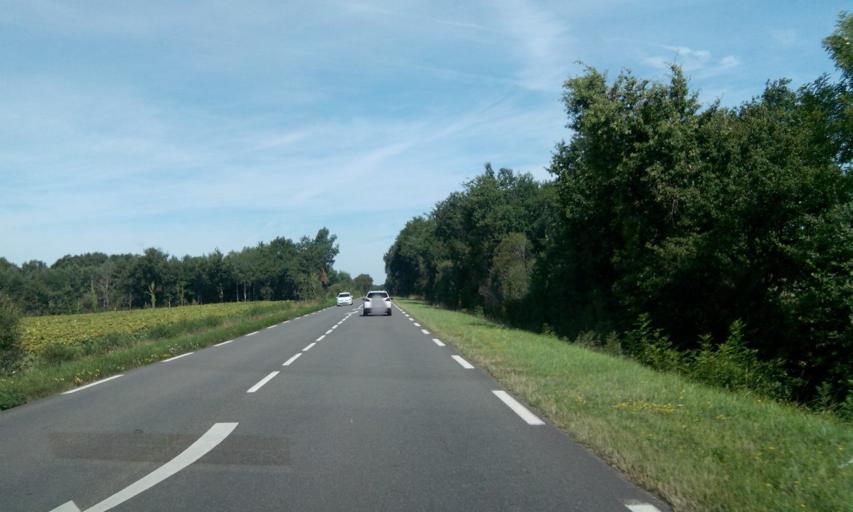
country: FR
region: Poitou-Charentes
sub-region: Departement de la Charente
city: Confolens
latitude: 46.0585
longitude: 0.6080
